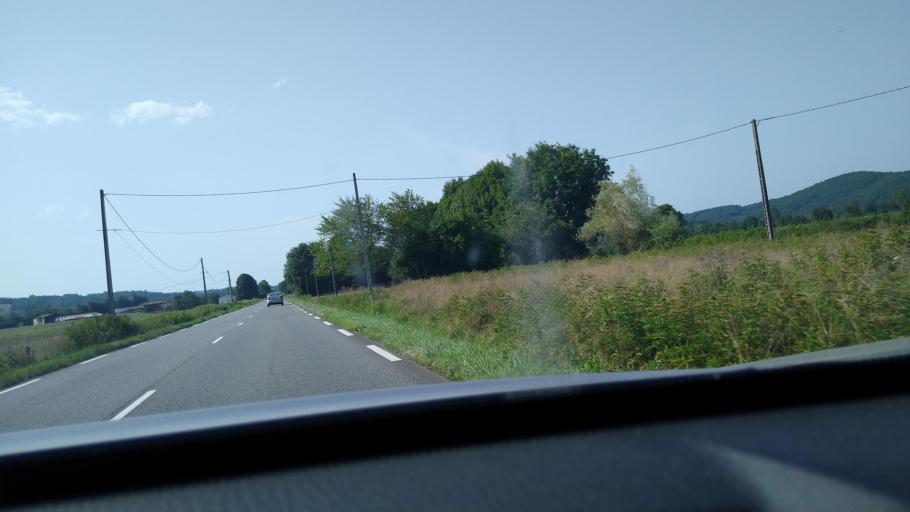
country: FR
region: Midi-Pyrenees
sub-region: Departement de la Haute-Garonne
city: Salies-du-Salat
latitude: 43.0429
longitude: 0.9907
